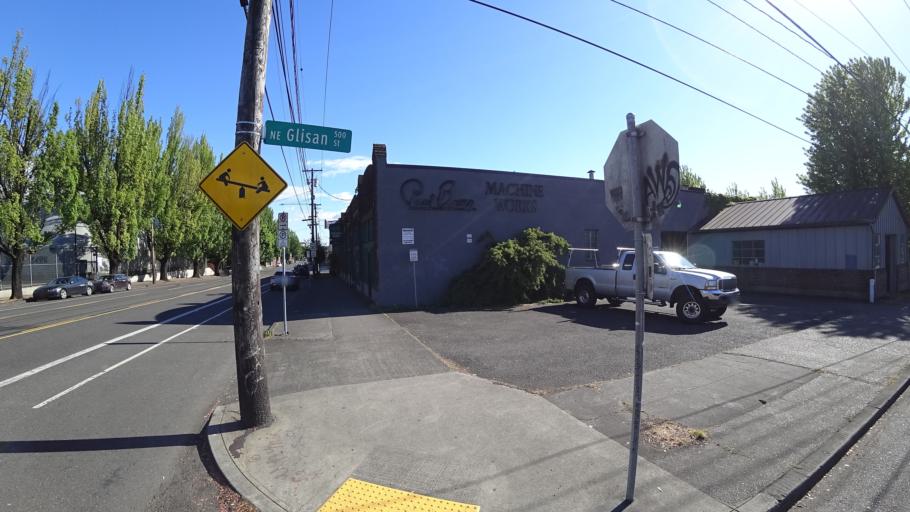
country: US
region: Oregon
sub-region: Multnomah County
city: Portland
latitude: 45.5265
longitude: -122.6538
